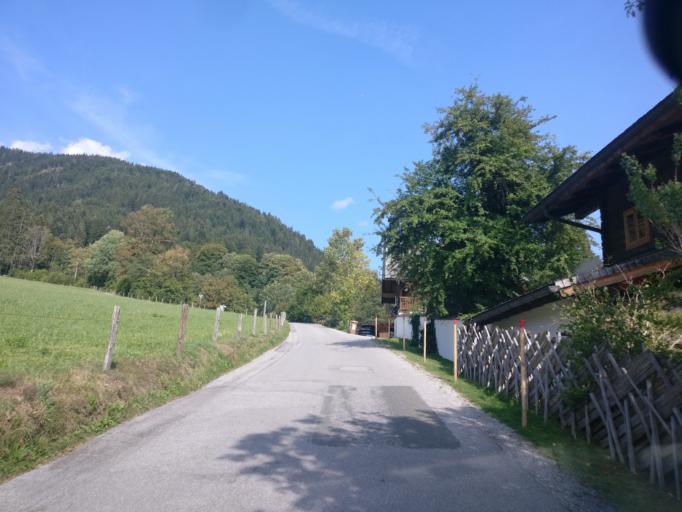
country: AT
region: Salzburg
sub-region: Politischer Bezirk Sankt Johann im Pongau
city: Werfenweng
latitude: 47.4633
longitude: 13.2382
